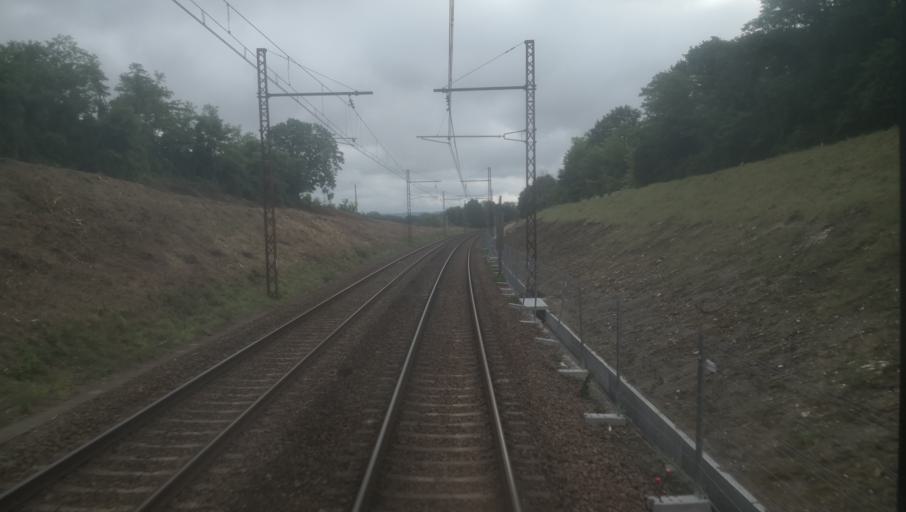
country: FR
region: Centre
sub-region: Departement du Cher
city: Vierzon
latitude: 47.1900
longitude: 2.0732
